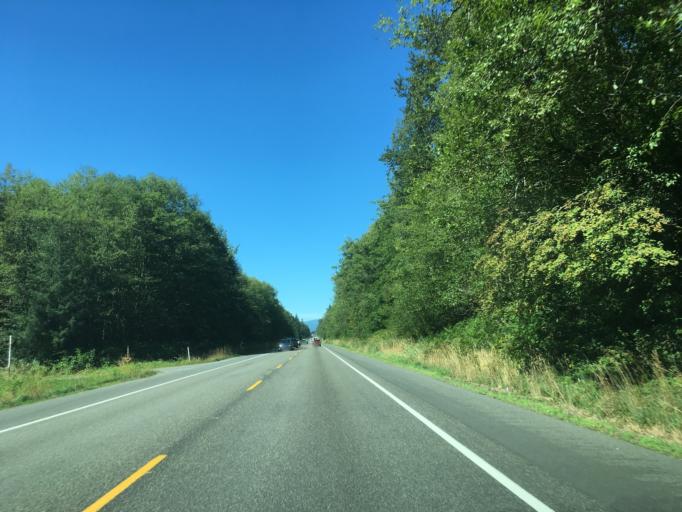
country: US
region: Washington
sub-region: Snohomish County
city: Sisco Heights
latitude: 48.1222
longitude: -122.1125
